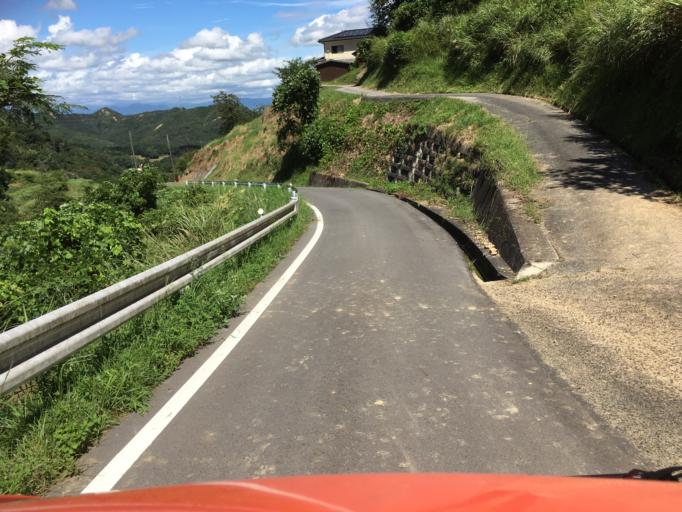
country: JP
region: Okayama
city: Tsuyama
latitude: 34.8967
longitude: 134.1381
